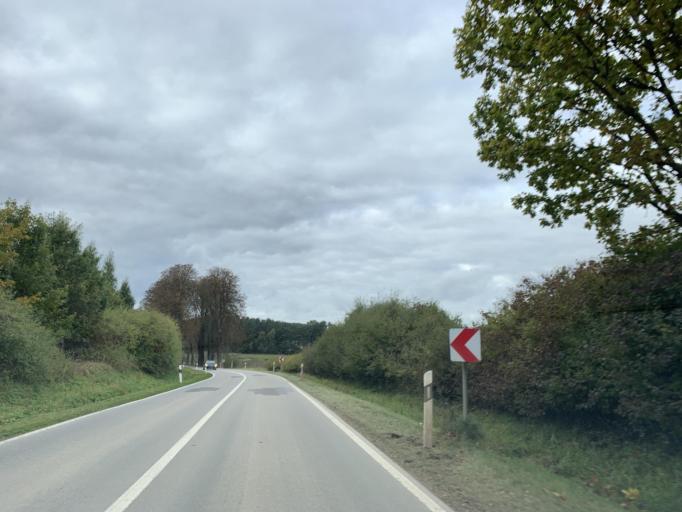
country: DE
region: Mecklenburg-Vorpommern
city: Blankensee
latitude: 53.3964
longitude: 13.2757
